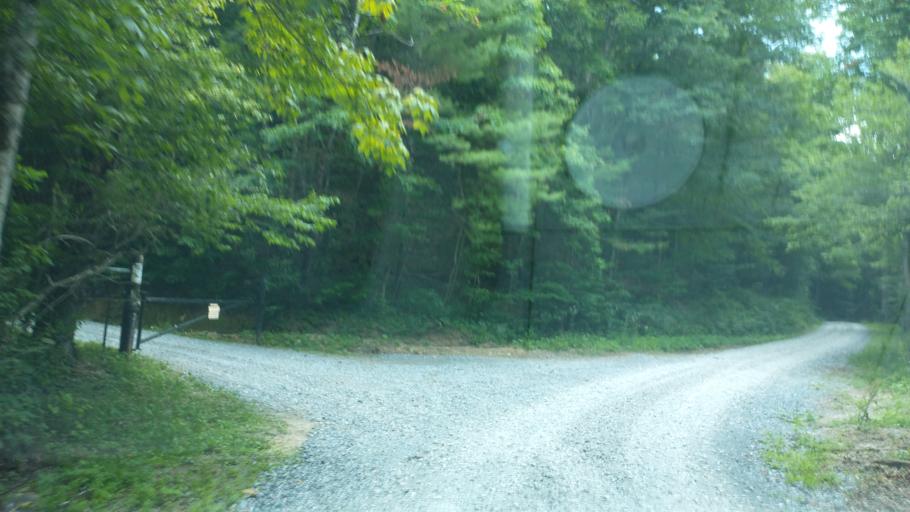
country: US
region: West Virginia
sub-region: Mercer County
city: Athens
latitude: 37.4340
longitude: -80.9980
